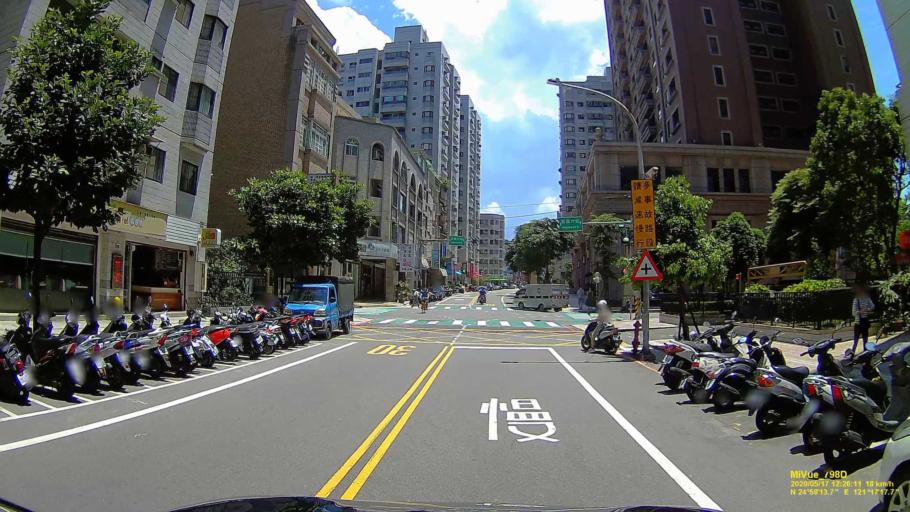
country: TW
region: Taiwan
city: Taoyuan City
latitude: 24.9870
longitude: 121.2883
